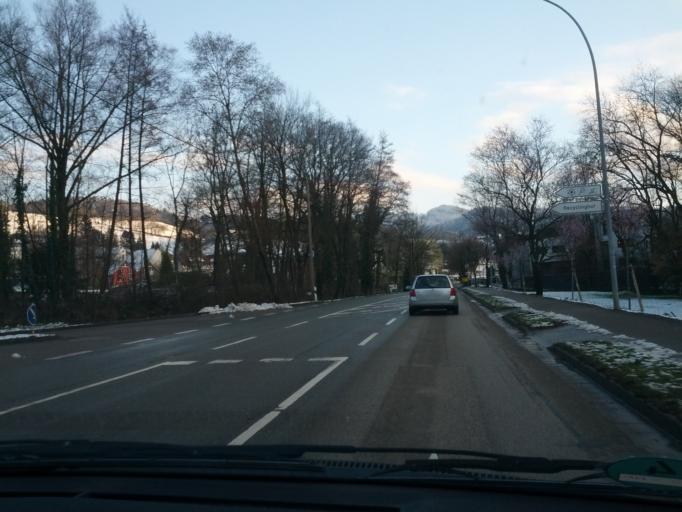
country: DE
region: Baden-Wuerttemberg
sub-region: Freiburg Region
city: Merzhausen
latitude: 47.9614
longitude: 7.8307
